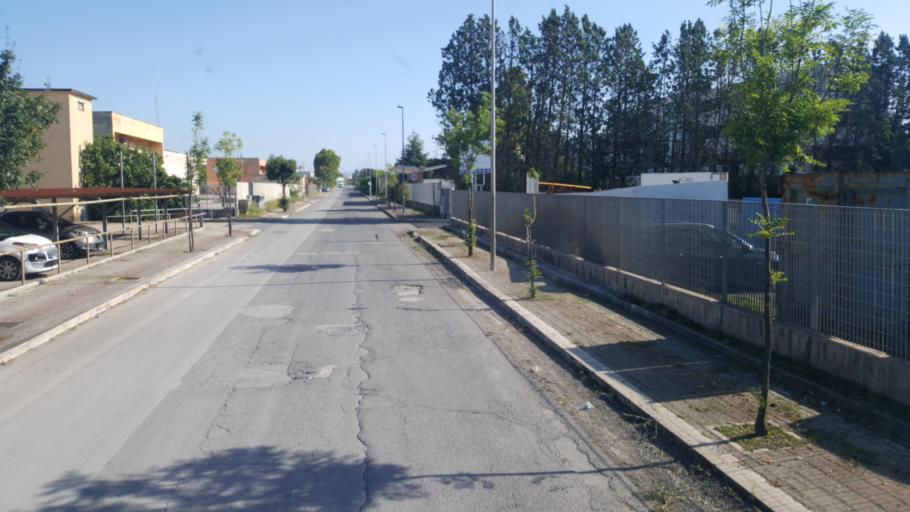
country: IT
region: Latium
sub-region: Provincia di Latina
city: Aprilia
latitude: 41.5747
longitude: 12.6468
